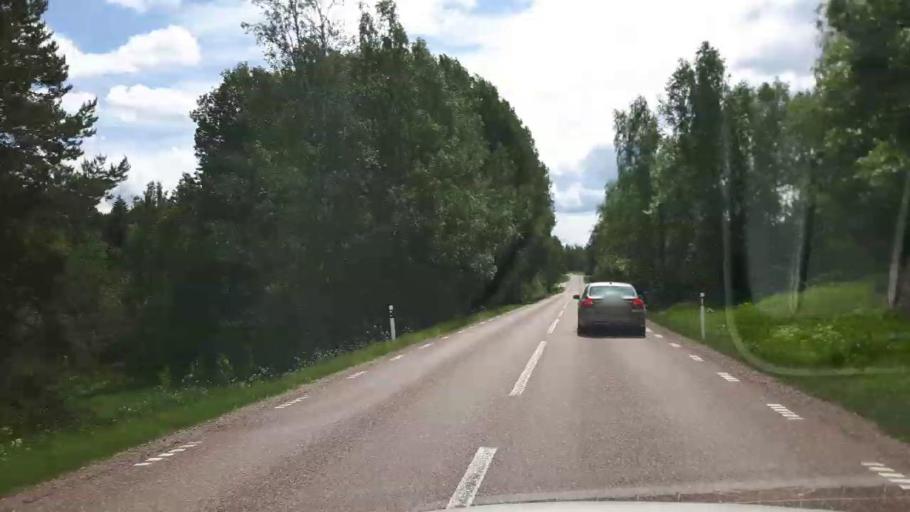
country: SE
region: Dalarna
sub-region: Saters Kommun
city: Saeter
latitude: 60.4196
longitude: 15.8469
